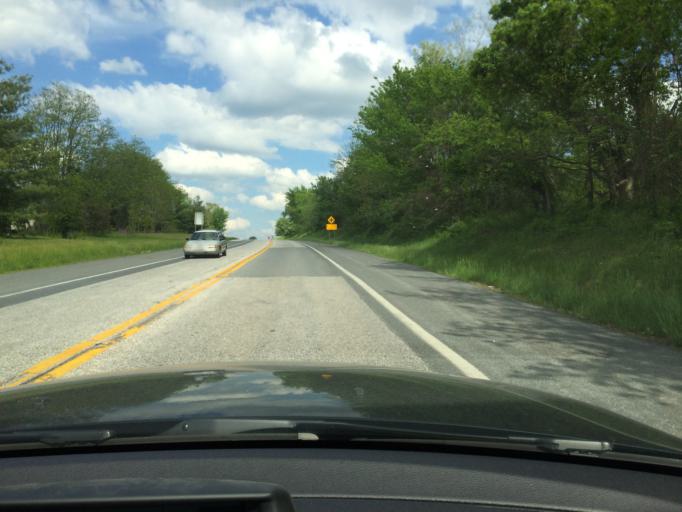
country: US
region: Maryland
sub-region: Carroll County
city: New Windsor
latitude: 39.5445
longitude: -77.0970
